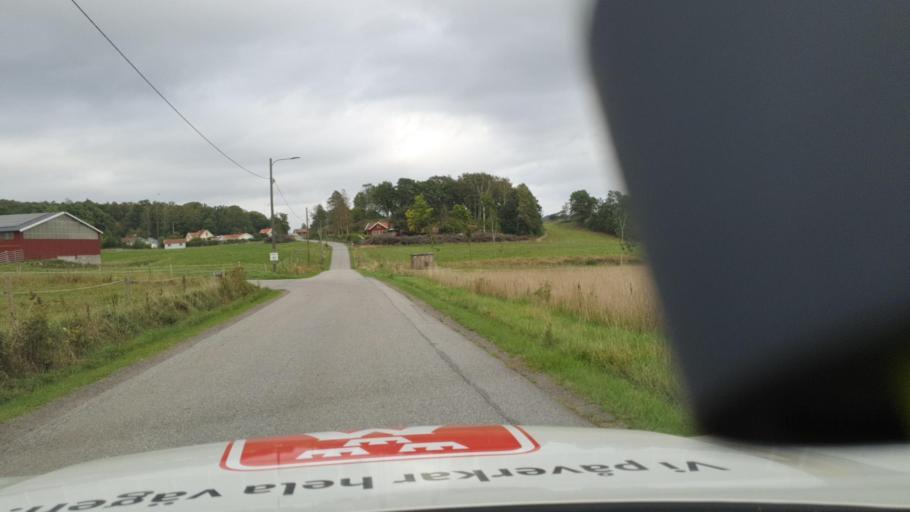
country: SE
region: Vaestra Goetaland
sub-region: Molndal
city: Lindome
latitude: 57.5864
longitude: 12.1027
